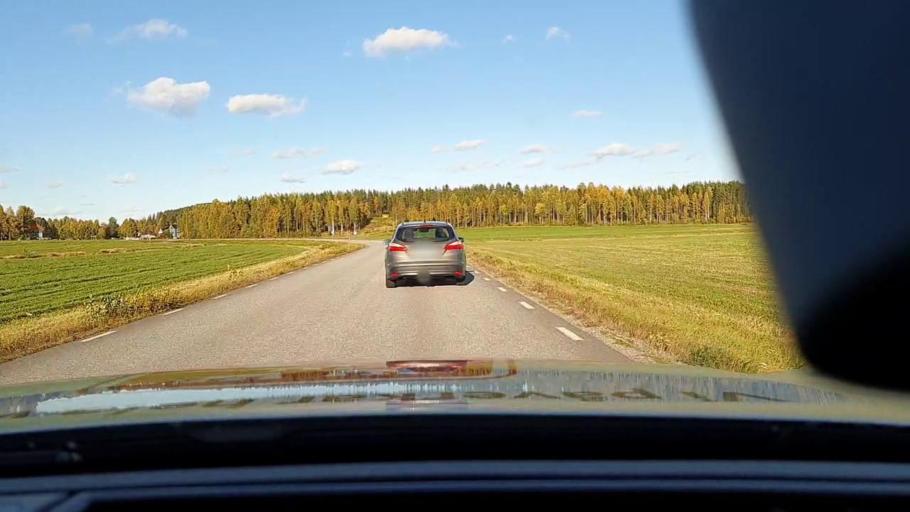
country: SE
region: Norrbotten
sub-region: Pitea Kommun
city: Norrfjarden
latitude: 65.5124
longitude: 21.4930
